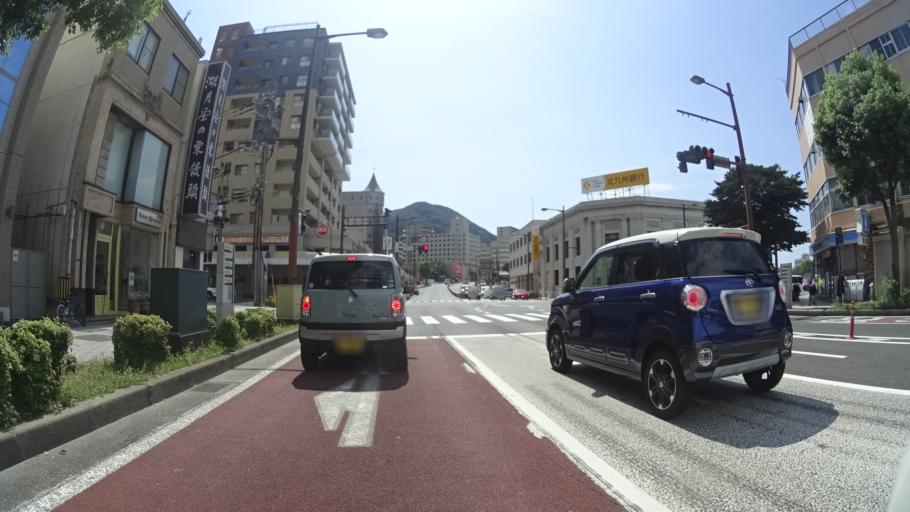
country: JP
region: Yamaguchi
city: Shimonoseki
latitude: 33.9447
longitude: 130.9643
